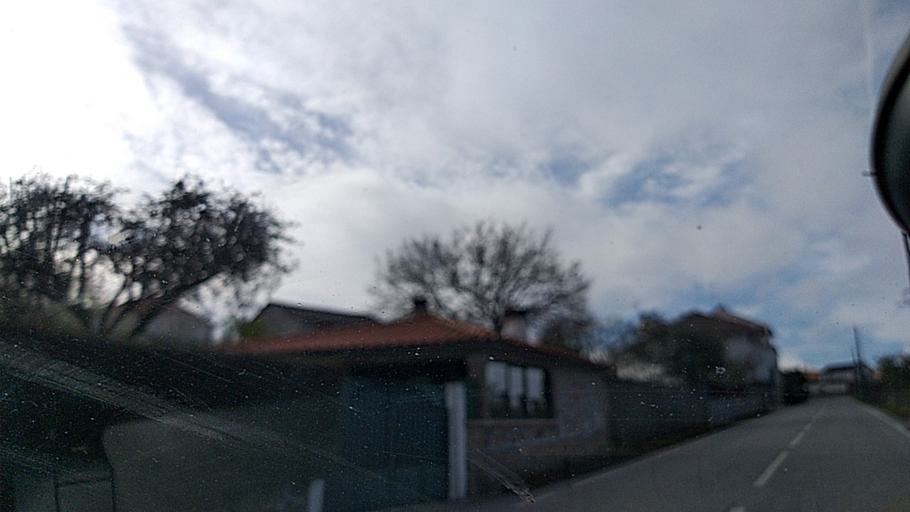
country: PT
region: Guarda
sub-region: Aguiar da Beira
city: Aguiar da Beira
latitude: 40.7611
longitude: -7.5411
